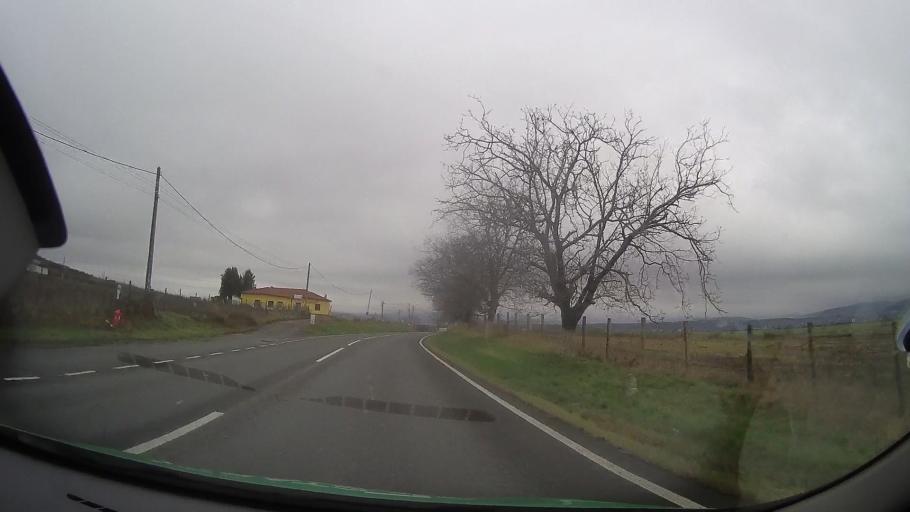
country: RO
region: Mures
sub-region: Municipiul Reghin
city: Apalina
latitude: 46.7613
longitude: 24.6723
